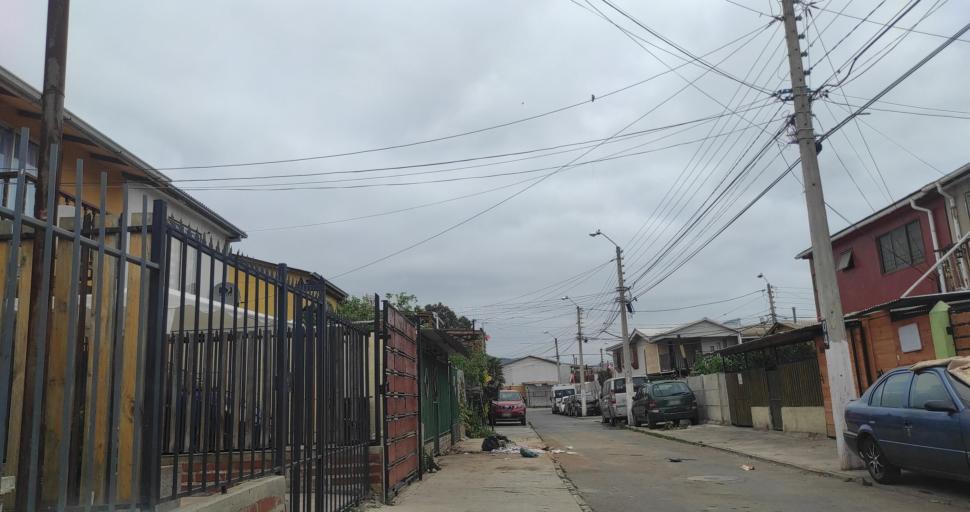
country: CL
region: Valparaiso
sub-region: Provincia de Marga Marga
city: Limache
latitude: -33.0198
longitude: -71.2631
